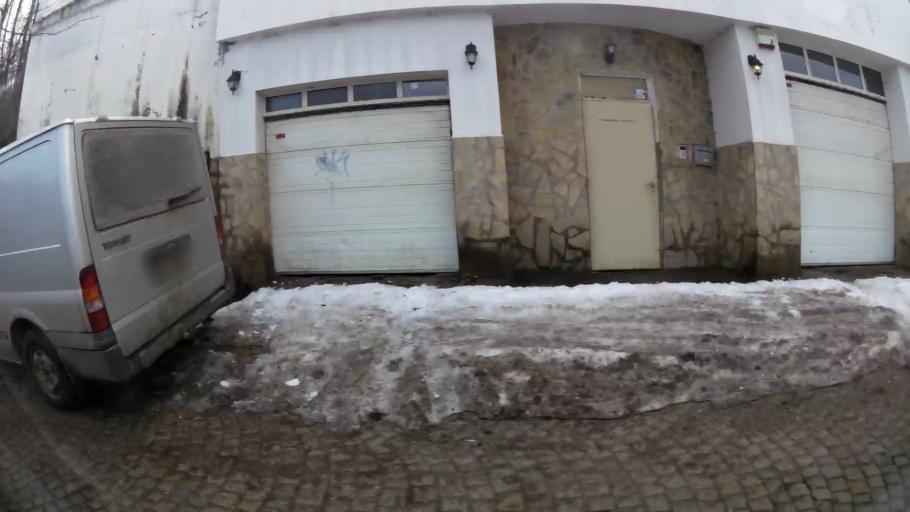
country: BG
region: Sofia-Capital
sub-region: Stolichna Obshtina
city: Sofia
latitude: 42.6454
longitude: 23.2741
